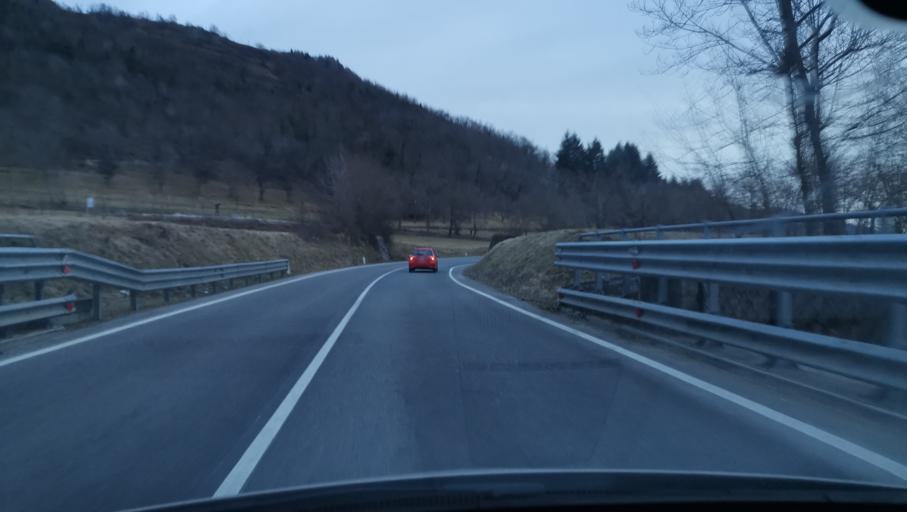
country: IT
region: Piedmont
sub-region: Provincia di Cuneo
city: Moiola
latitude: 44.3313
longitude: 7.3964
